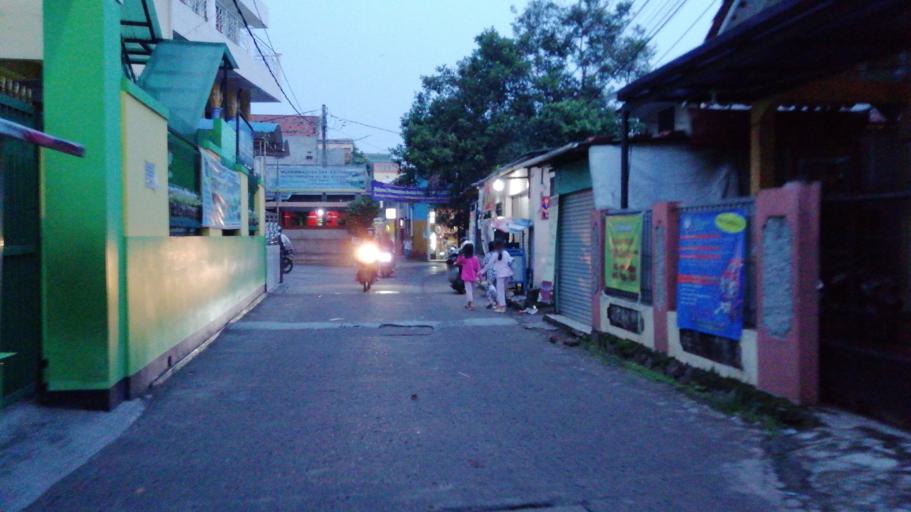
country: ID
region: West Java
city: Depok
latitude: -6.3593
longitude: 106.8337
